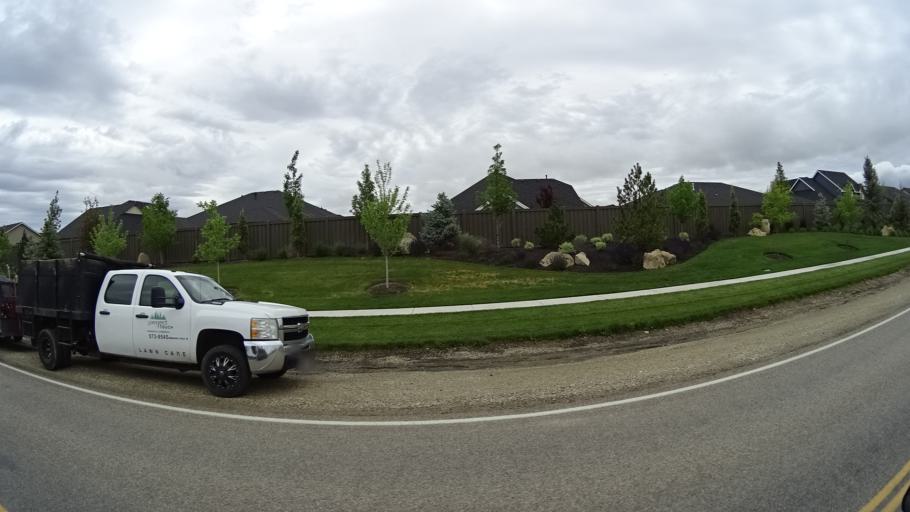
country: US
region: Idaho
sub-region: Ada County
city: Eagle
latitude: 43.7063
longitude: -116.4206
